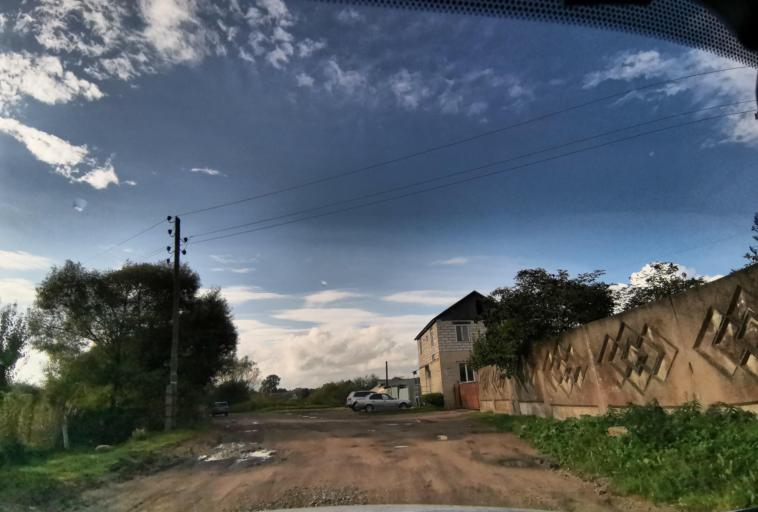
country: RU
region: Kaliningrad
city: Chernyakhovsk
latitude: 54.6577
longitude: 21.8354
